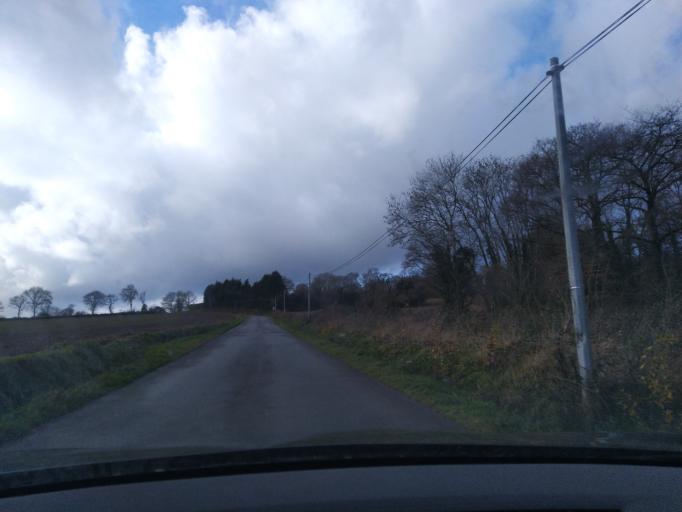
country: FR
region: Brittany
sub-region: Departement du Finistere
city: Guerlesquin
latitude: 48.4297
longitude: -3.6094
